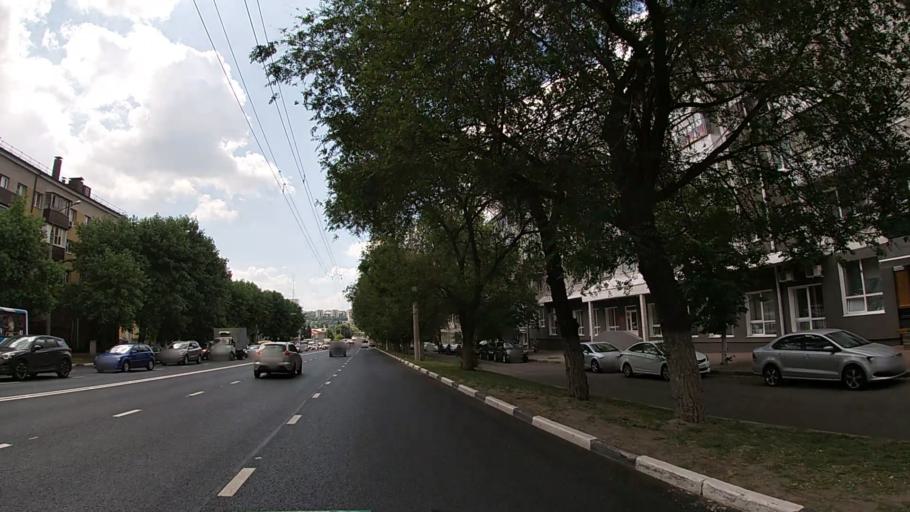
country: RU
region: Belgorod
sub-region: Belgorodskiy Rayon
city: Belgorod
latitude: 50.5980
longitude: 36.5799
